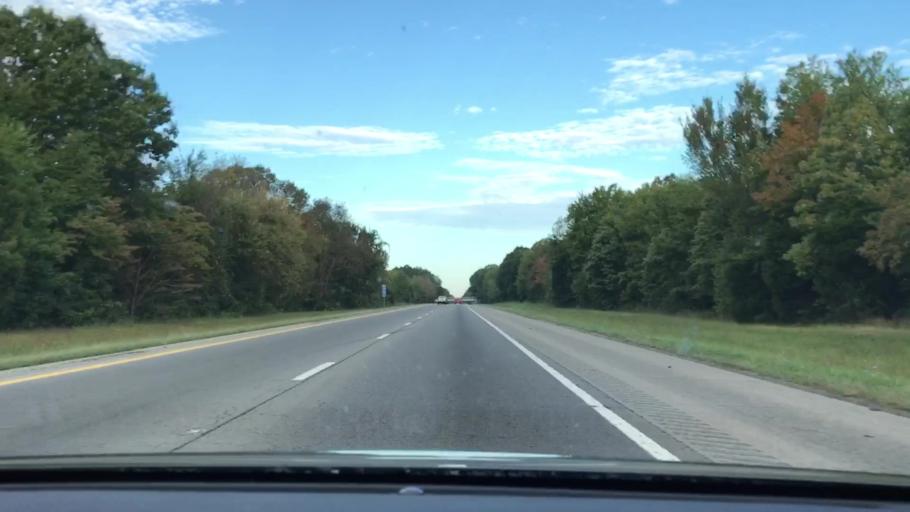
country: US
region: Tennessee
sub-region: Cheatham County
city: Pleasant View
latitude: 36.4284
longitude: -87.0659
